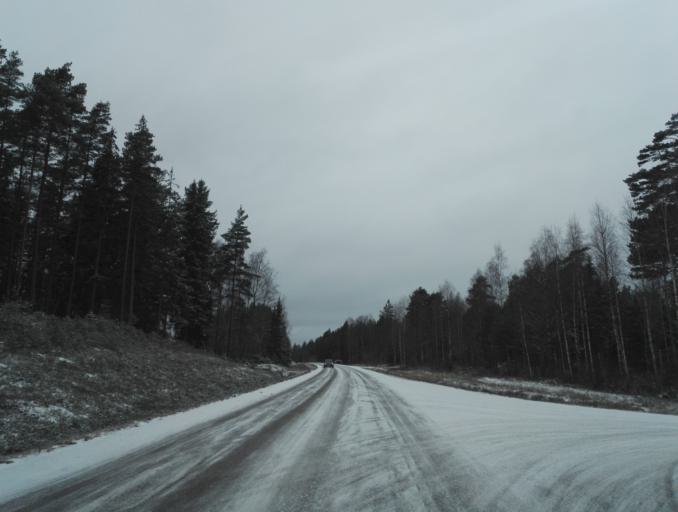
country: SE
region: Kronoberg
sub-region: Lessebo Kommun
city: Lessebo
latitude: 56.7389
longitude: 15.2524
